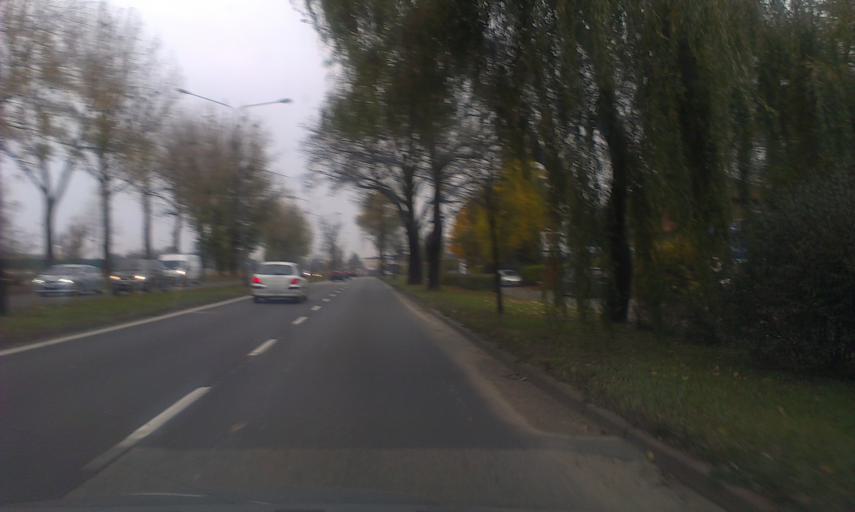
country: PL
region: Greater Poland Voivodeship
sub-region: Powiat poznanski
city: Suchy Las
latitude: 52.4251
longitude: 16.8627
